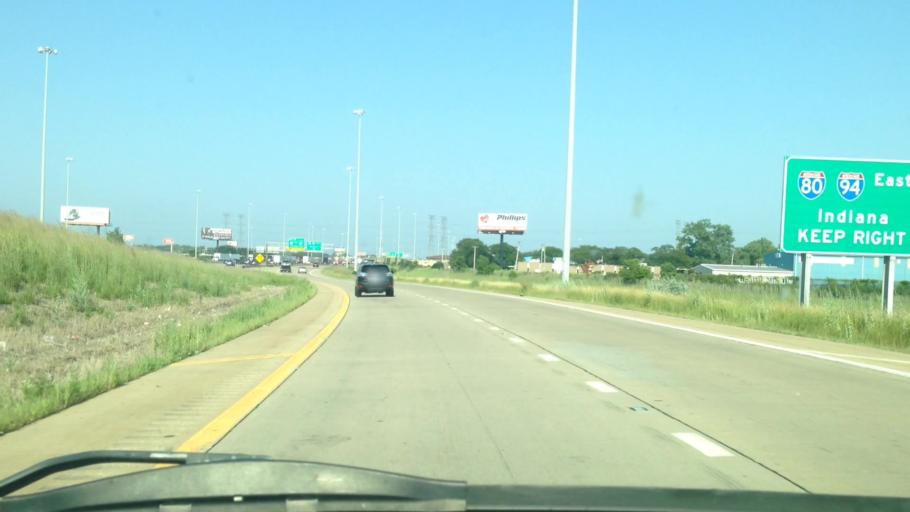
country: US
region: Illinois
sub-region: Cook County
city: Lansing
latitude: 41.5767
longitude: -87.5723
